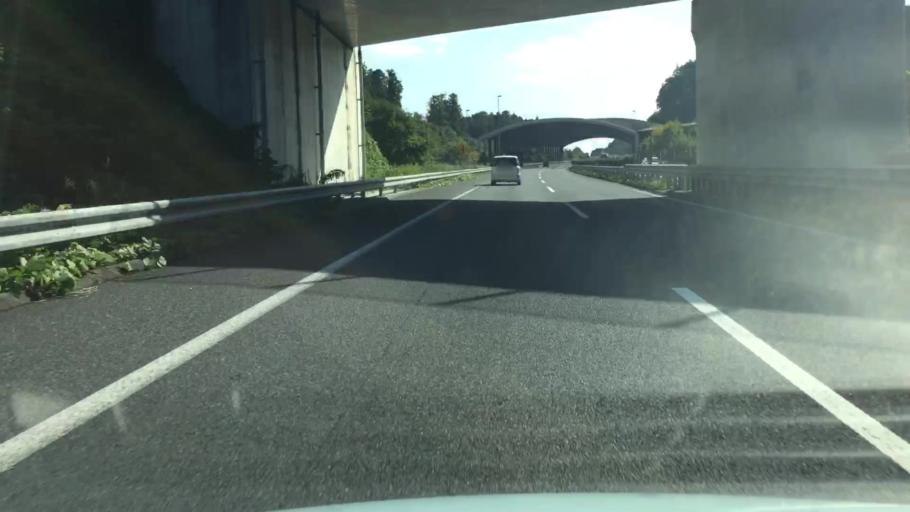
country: JP
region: Ibaraki
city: Tomobe
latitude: 36.3401
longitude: 140.2729
